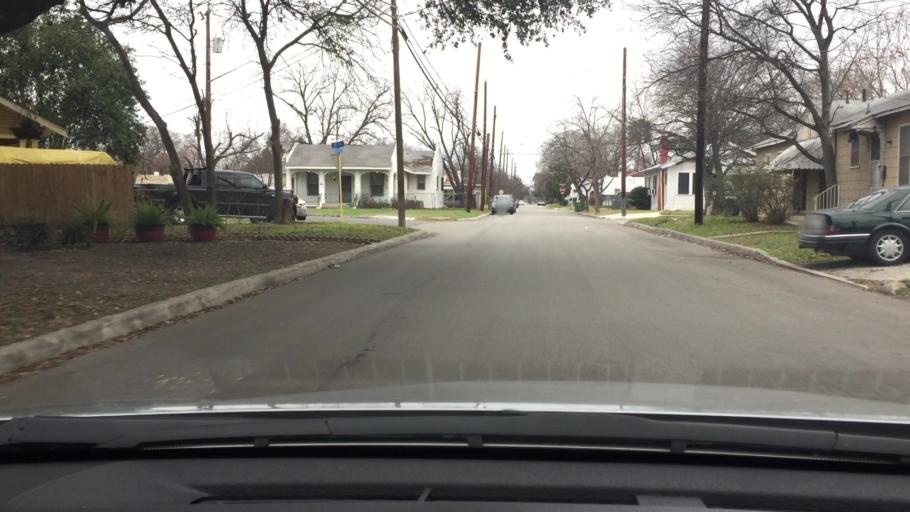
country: US
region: Texas
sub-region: Bexar County
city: Olmos Park
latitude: 29.4603
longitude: -98.5209
